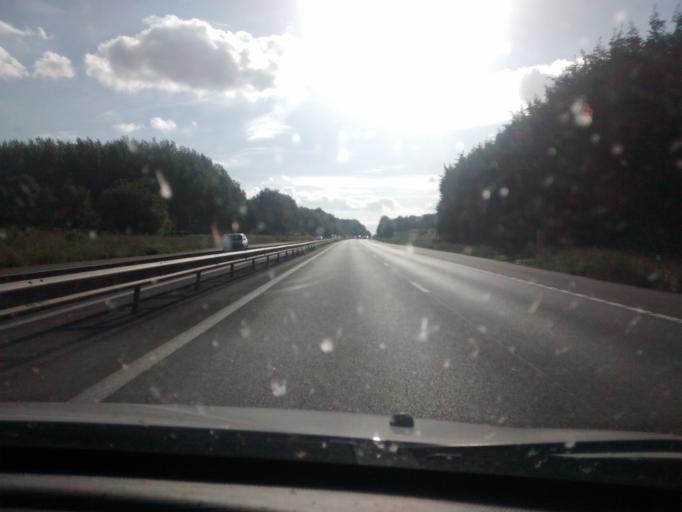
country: FR
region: Brittany
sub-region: Departement d'Ille-et-Vilaine
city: Louvigne-de-Bais
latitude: 48.0766
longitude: -1.3041
